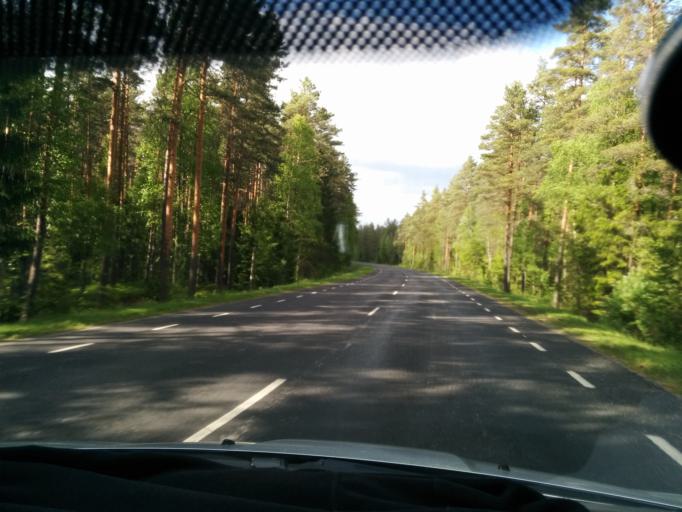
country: EE
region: Harju
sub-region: Loksa linn
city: Loksa
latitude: 59.5431
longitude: 25.7374
